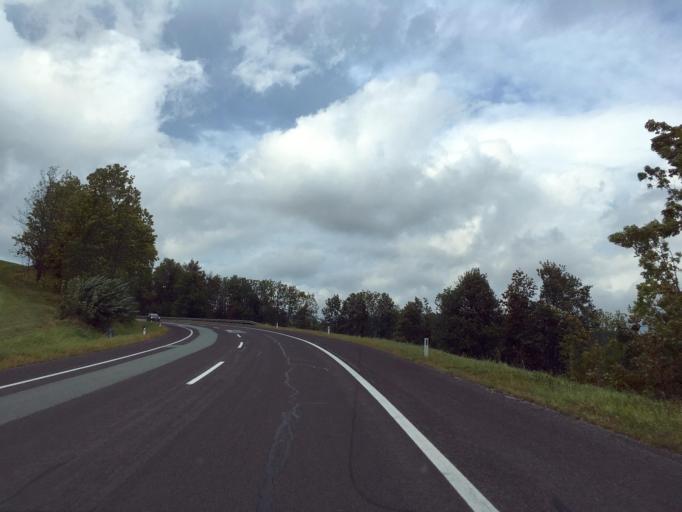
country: AT
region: Lower Austria
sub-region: Politischer Bezirk Neunkirchen
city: Monichkirchen
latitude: 47.4898
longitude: 16.0416
